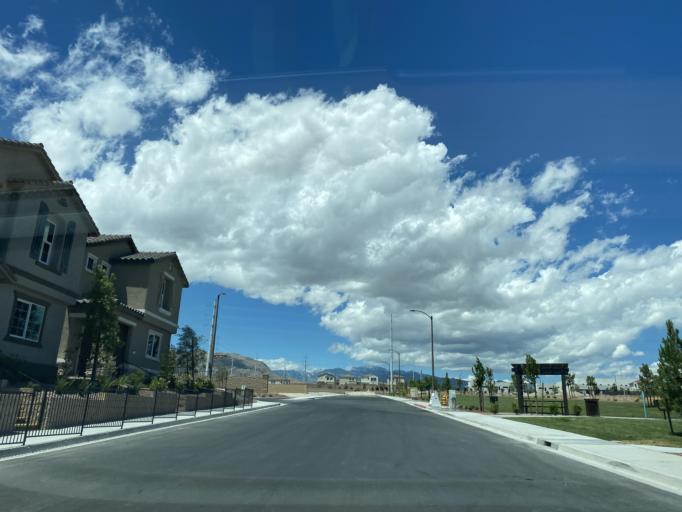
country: US
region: Nevada
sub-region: Clark County
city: Summerlin South
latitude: 36.3074
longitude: -115.3254
